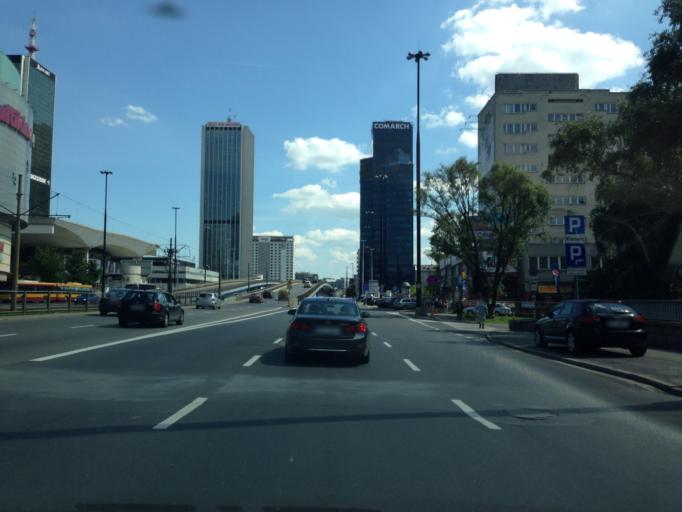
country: PL
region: Masovian Voivodeship
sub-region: Warszawa
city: Warsaw
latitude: 52.2302
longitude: 21.0001
